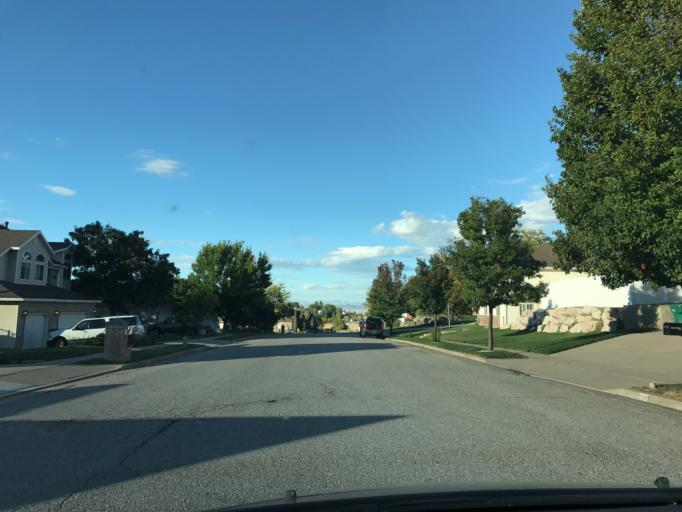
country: US
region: Utah
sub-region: Davis County
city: South Weber
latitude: 41.1069
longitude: -111.9245
